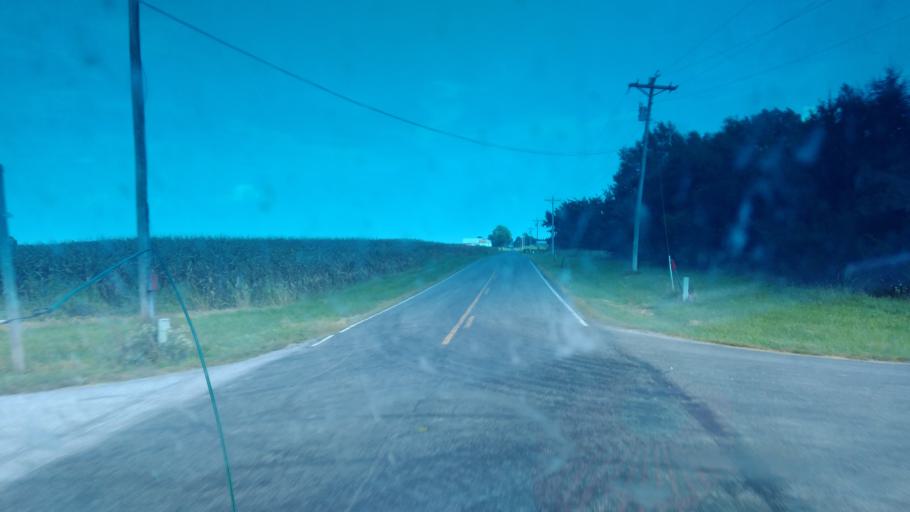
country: US
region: Ohio
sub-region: Hardin County
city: Forest
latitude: 40.9050
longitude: -83.5006
